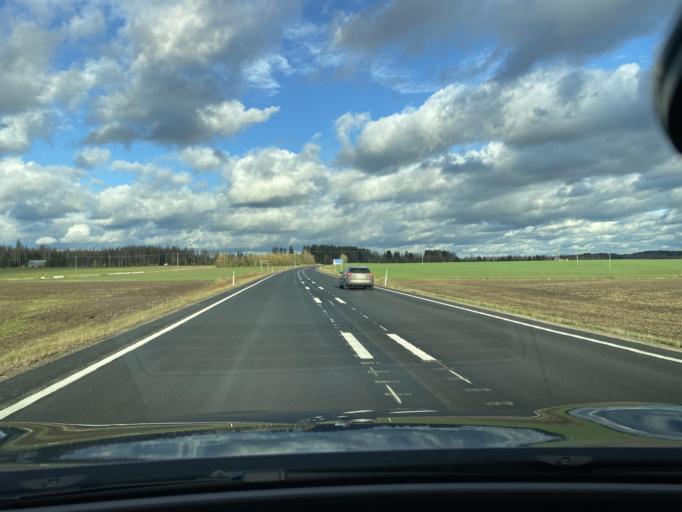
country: FI
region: Haeme
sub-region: Riihimaeki
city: Oitti
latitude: 60.8313
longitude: 25.0824
